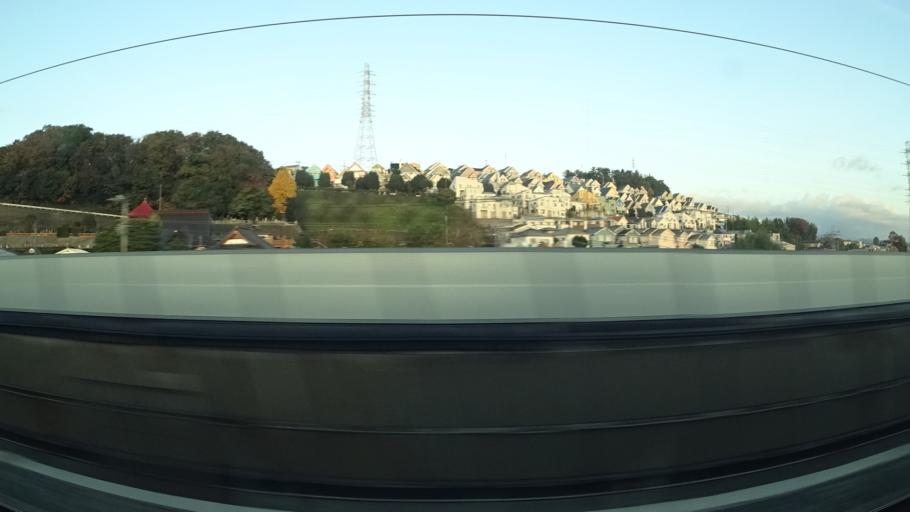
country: JP
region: Kanagawa
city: Oiso
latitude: 35.3384
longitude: 139.3039
